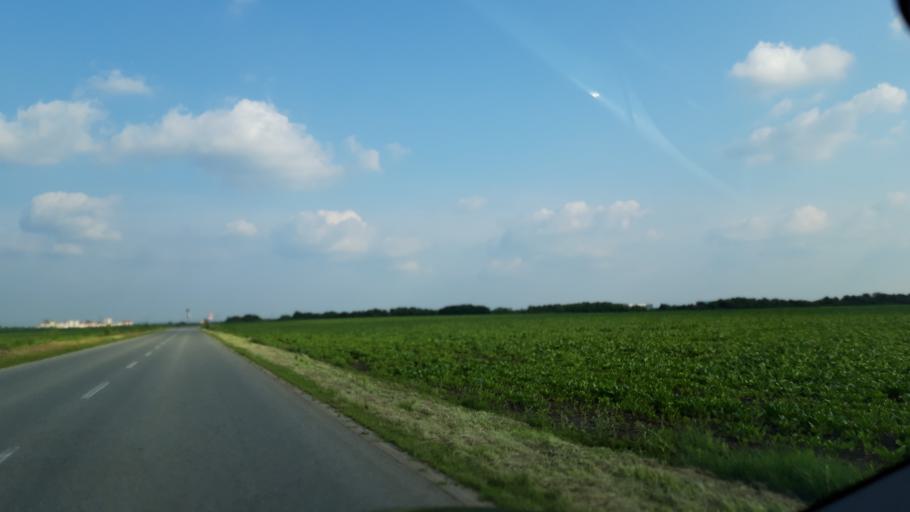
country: RS
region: Autonomna Pokrajina Vojvodina
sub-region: Sremski Okrug
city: Ingija
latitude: 45.0786
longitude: 20.1207
